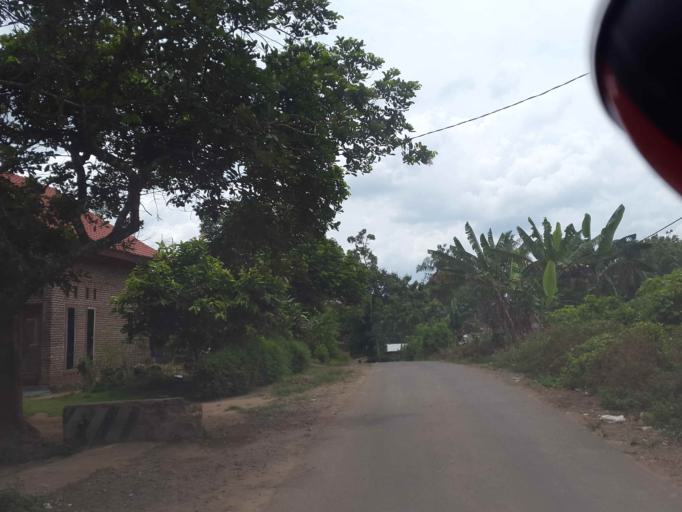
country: ID
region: Lampung
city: Natar
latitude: -5.3158
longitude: 105.2416
